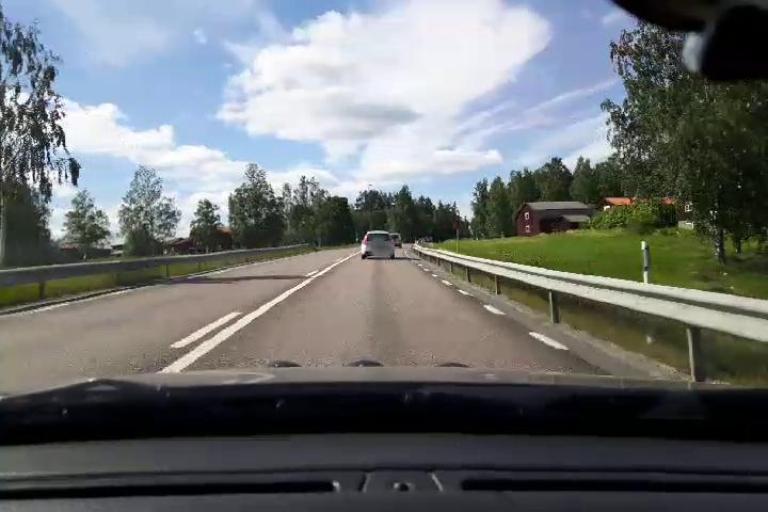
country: SE
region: Gaevleborg
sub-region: Bollnas Kommun
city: Bollnas
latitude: 61.3251
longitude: 16.4179
